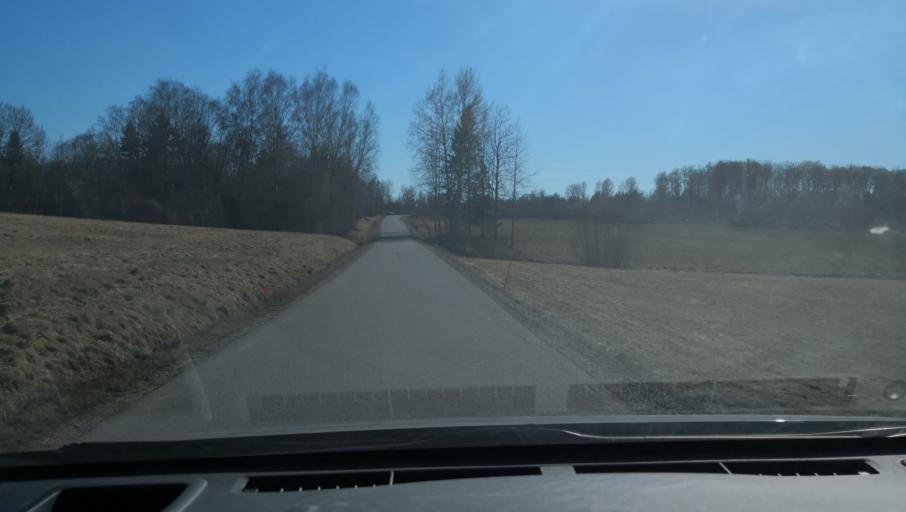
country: SE
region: Dalarna
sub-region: Avesta Kommun
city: Avesta
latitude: 60.0738
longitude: 16.3791
